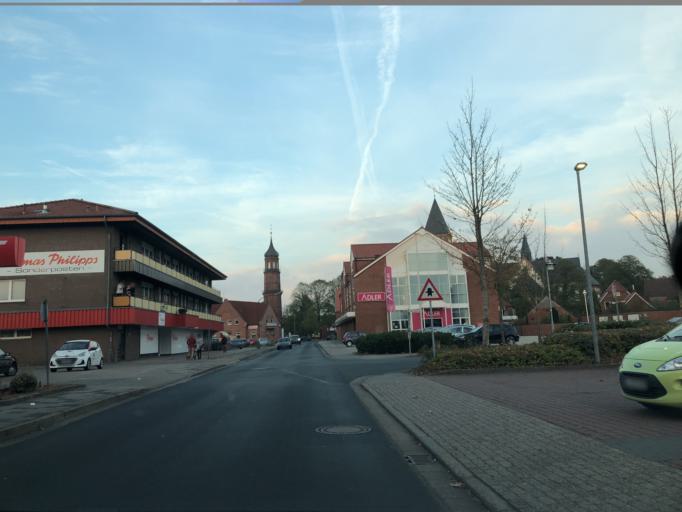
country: DE
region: Lower Saxony
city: Papenburg
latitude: 53.0729
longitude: 7.4396
